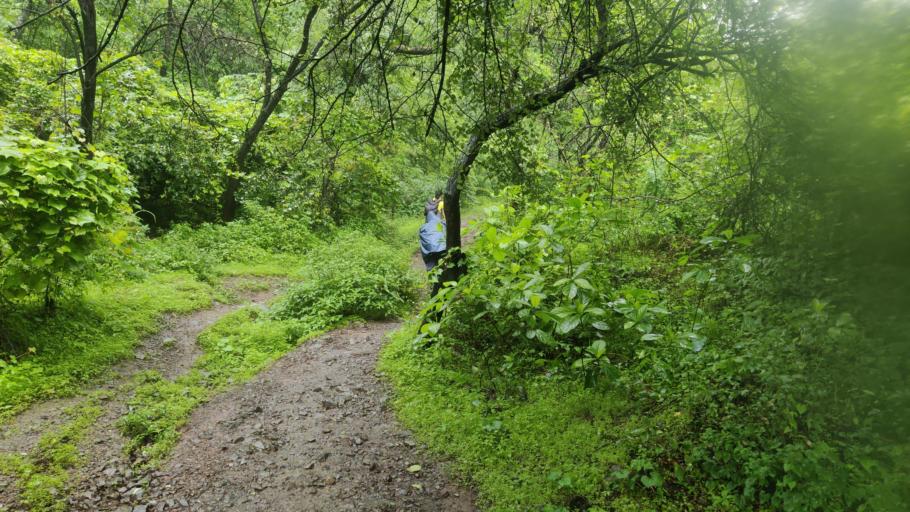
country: IN
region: Maharashtra
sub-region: Thane
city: Thane
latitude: 19.2378
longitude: 72.9619
